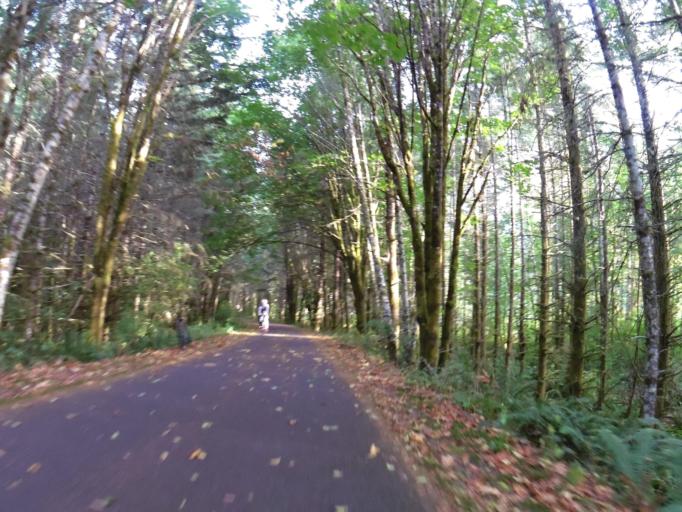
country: US
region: Washington
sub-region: Thurston County
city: Tenino
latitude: 46.9289
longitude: -122.8213
